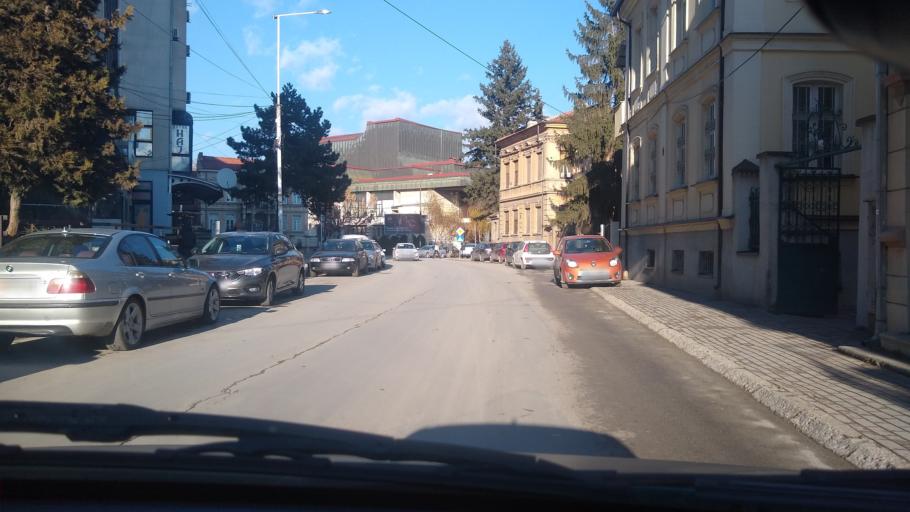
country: MK
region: Bitola
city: Bitola
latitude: 41.0268
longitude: 21.3339
